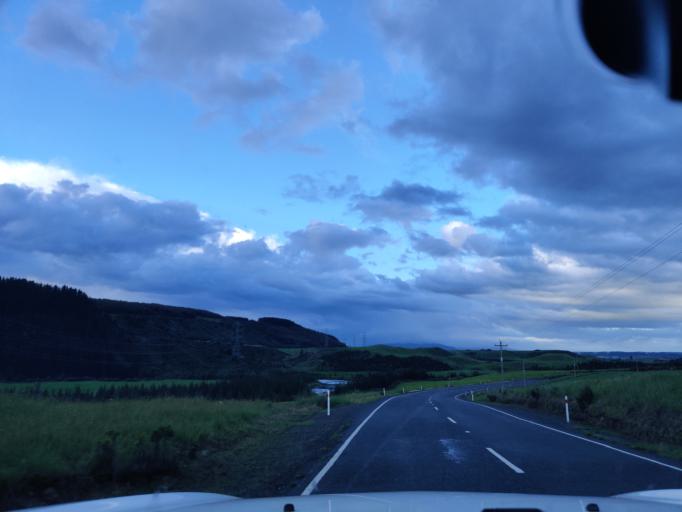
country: NZ
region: Waikato
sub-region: South Waikato District
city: Tokoroa
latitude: -38.3724
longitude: 175.8017
